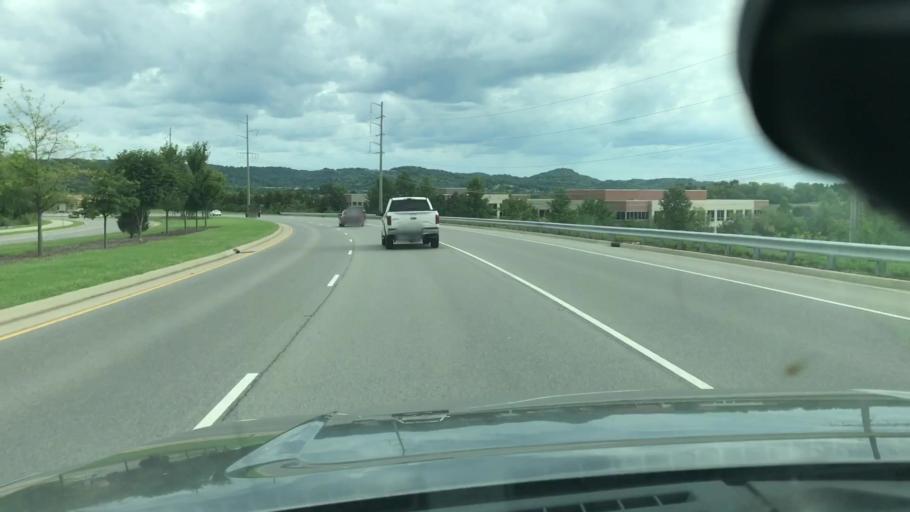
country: US
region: Tennessee
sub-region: Williamson County
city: Franklin
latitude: 35.9377
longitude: -86.8380
